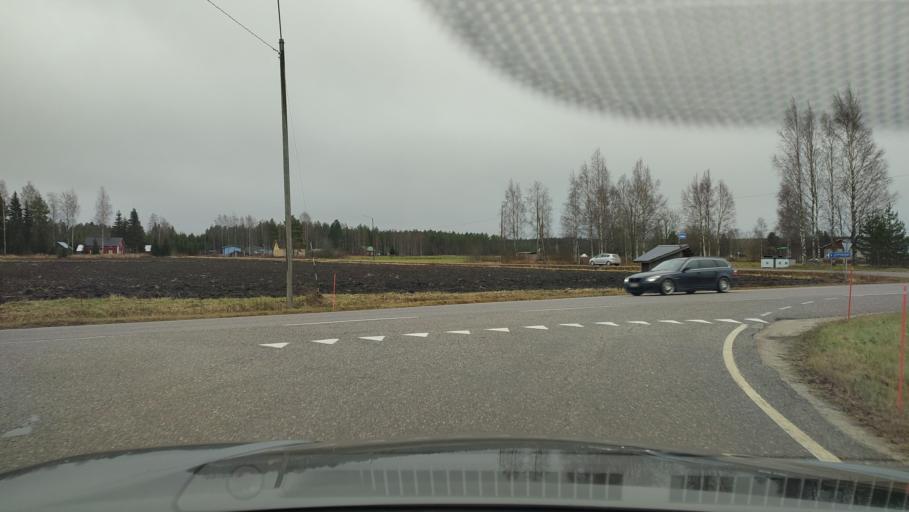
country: FI
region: Southern Ostrobothnia
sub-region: Suupohja
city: Isojoki
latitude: 62.1900
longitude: 21.9819
